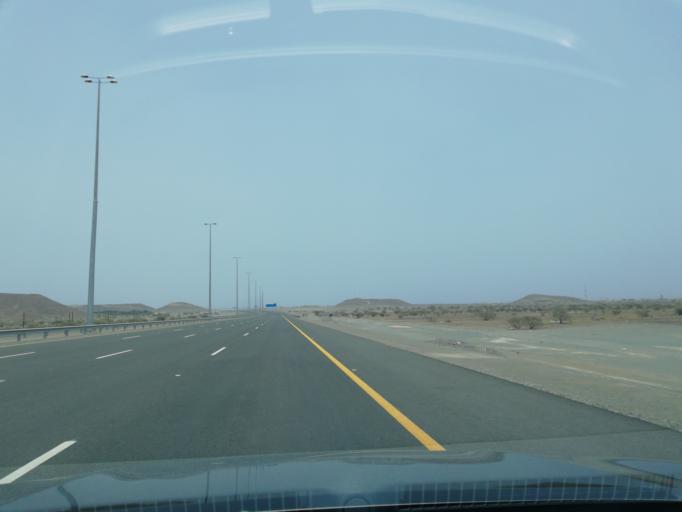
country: OM
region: Al Batinah
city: Al Liwa'
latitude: 24.5085
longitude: 56.5057
